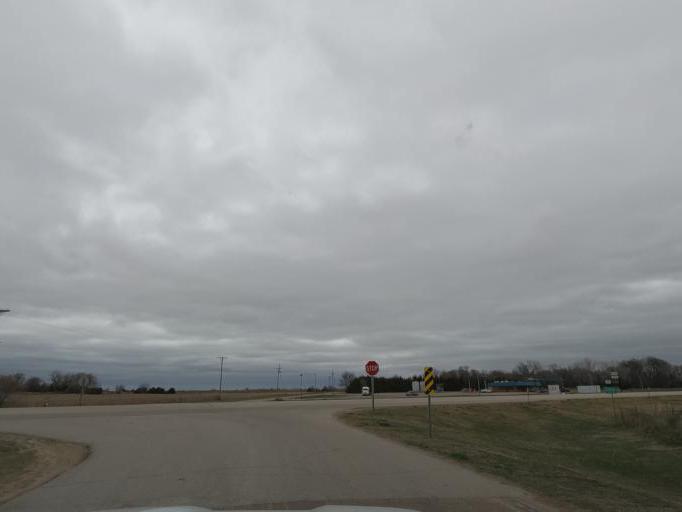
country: US
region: Kansas
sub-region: Stafford County
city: Stafford
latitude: 37.9671
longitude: -98.4079
